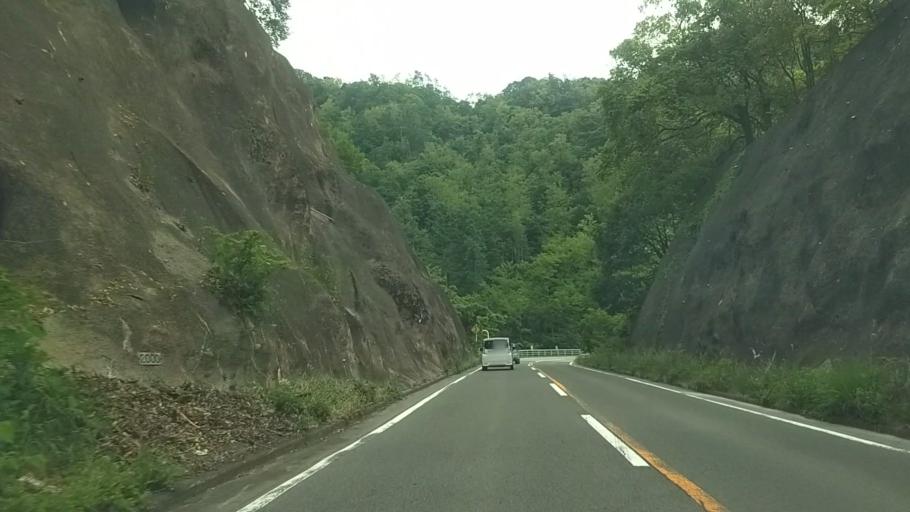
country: JP
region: Yamanashi
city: Isawa
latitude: 35.5649
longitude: 138.5940
